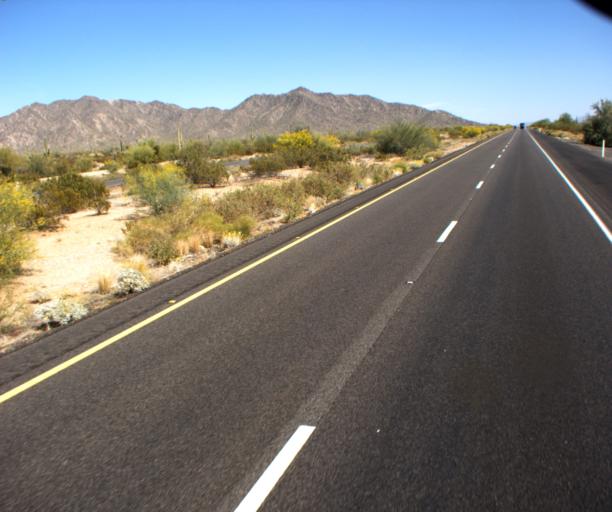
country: US
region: Arizona
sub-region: Maricopa County
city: Gila Bend
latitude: 32.8708
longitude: -112.4357
